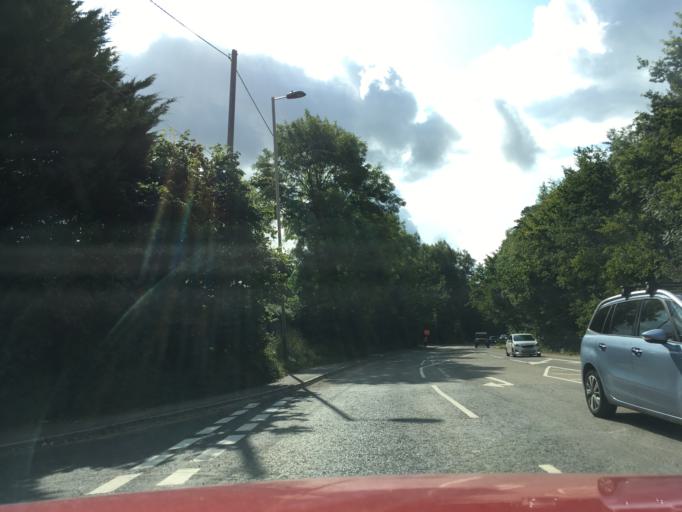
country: GB
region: England
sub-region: Hampshire
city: Bishops Waltham
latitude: 50.9510
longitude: -1.2092
